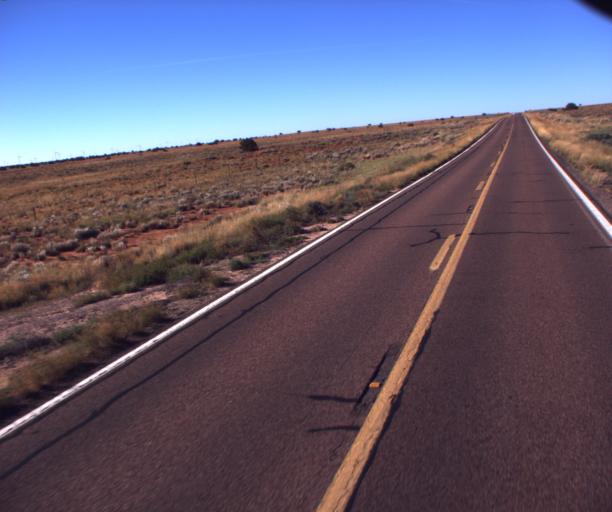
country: US
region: Arizona
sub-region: Navajo County
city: Holbrook
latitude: 34.7319
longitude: -110.2813
